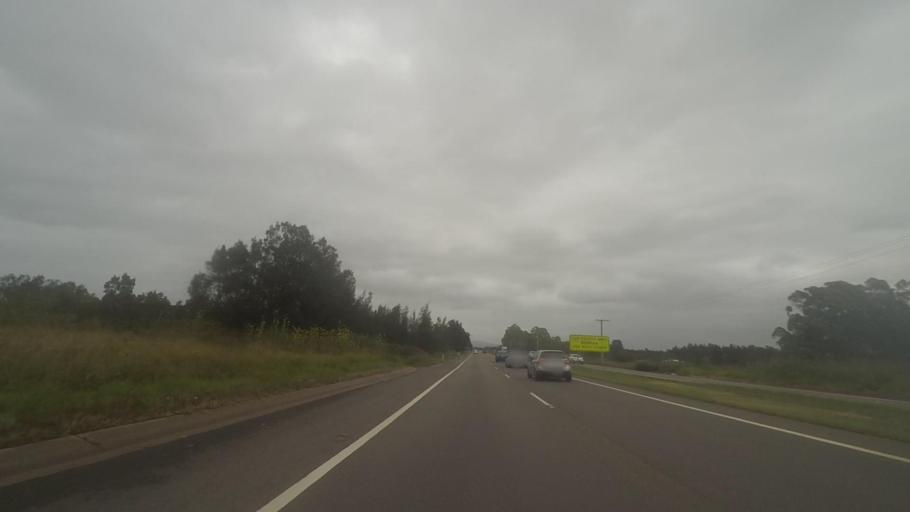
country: AU
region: New South Wales
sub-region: Newcastle
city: Beresfield
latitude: -32.8137
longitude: 151.7024
